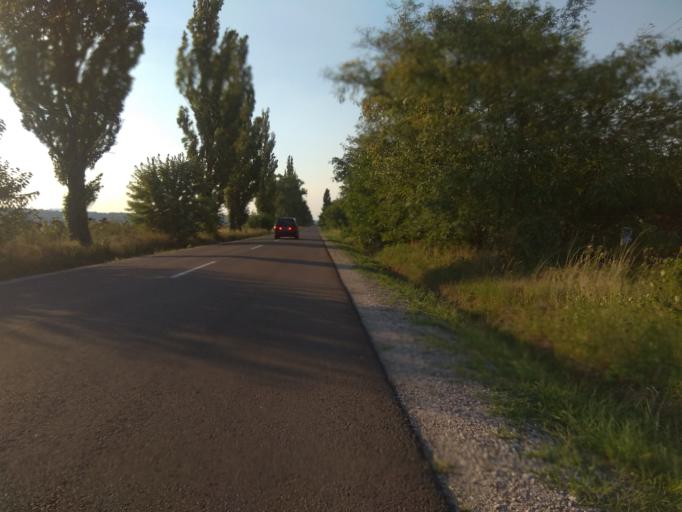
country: HU
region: Borsod-Abauj-Zemplen
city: Nyekladhaza
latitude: 47.9728
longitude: 20.8515
